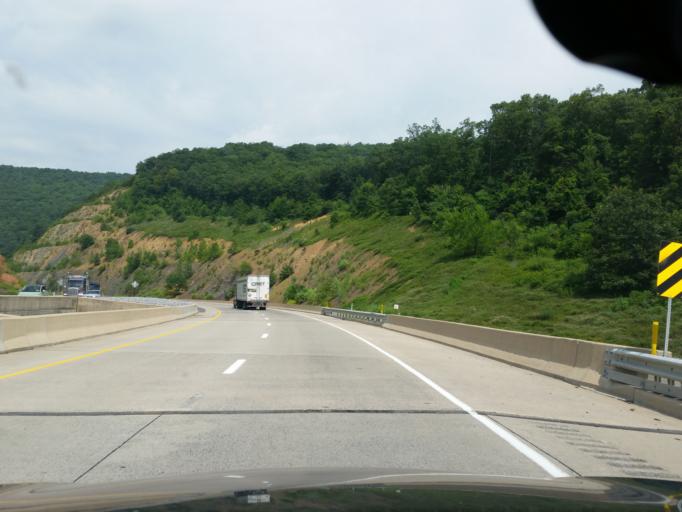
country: US
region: Pennsylvania
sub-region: Mifflin County
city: Milroy
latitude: 40.7296
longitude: -77.6059
